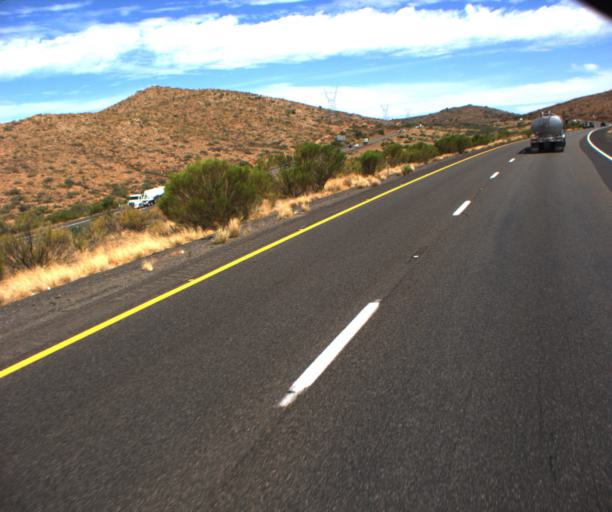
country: US
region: Arizona
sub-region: Yavapai County
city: Cordes Lakes
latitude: 34.2893
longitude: -112.1234
